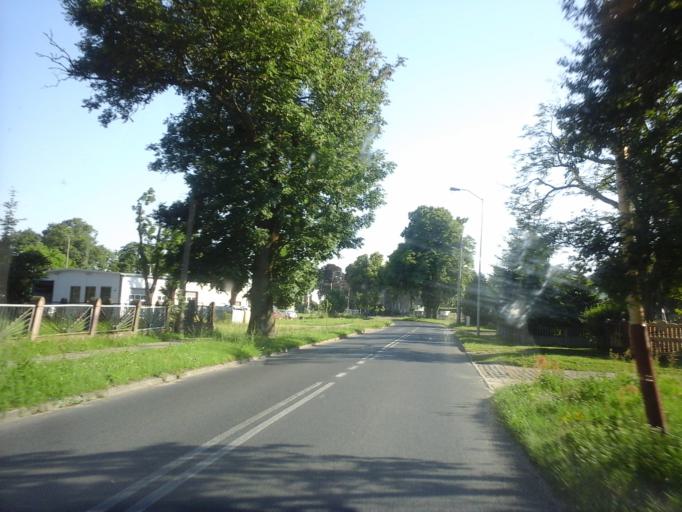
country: PL
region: West Pomeranian Voivodeship
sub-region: Powiat stargardzki
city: Chociwel
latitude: 53.4707
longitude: 15.3338
